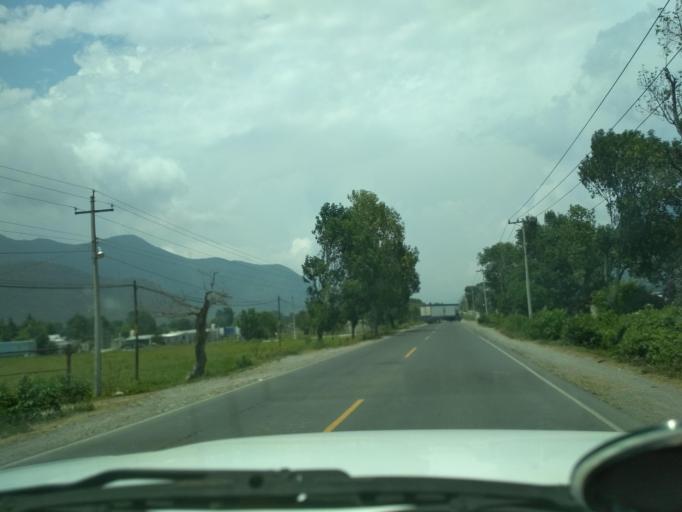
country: MX
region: Veracruz
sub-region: Nogales
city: Taza de Agua Ojo Zarco
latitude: 18.7706
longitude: -97.2172
